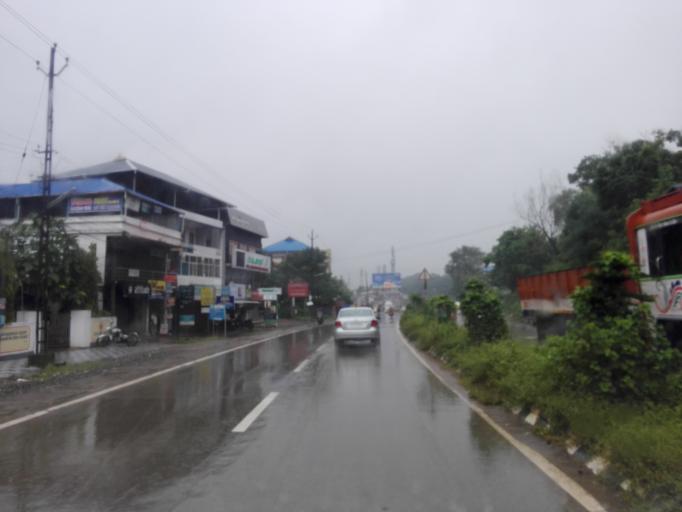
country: IN
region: Kerala
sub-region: Ernakulam
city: Elur
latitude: 10.0542
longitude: 76.3269
